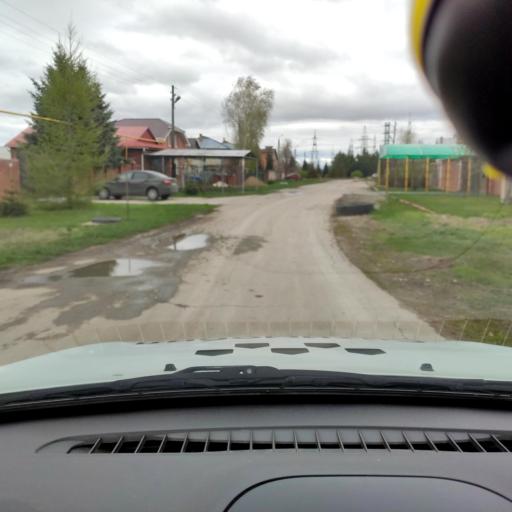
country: RU
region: Samara
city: Tol'yatti
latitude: 53.5839
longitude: 49.3307
